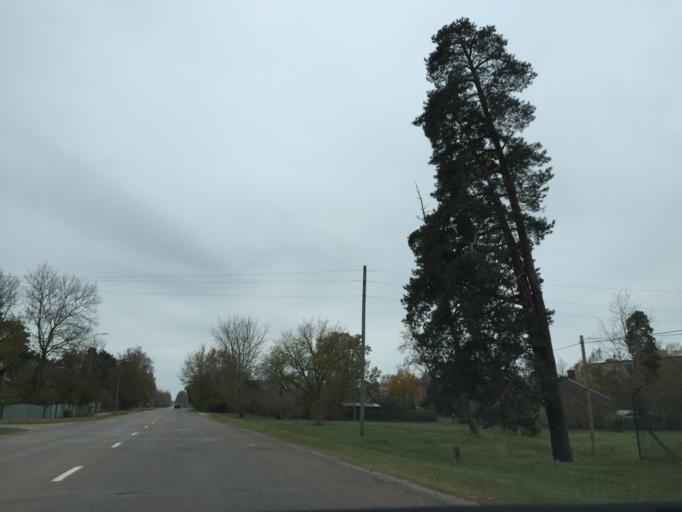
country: LV
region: Marupe
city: Marupe
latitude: 56.8854
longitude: 24.0703
